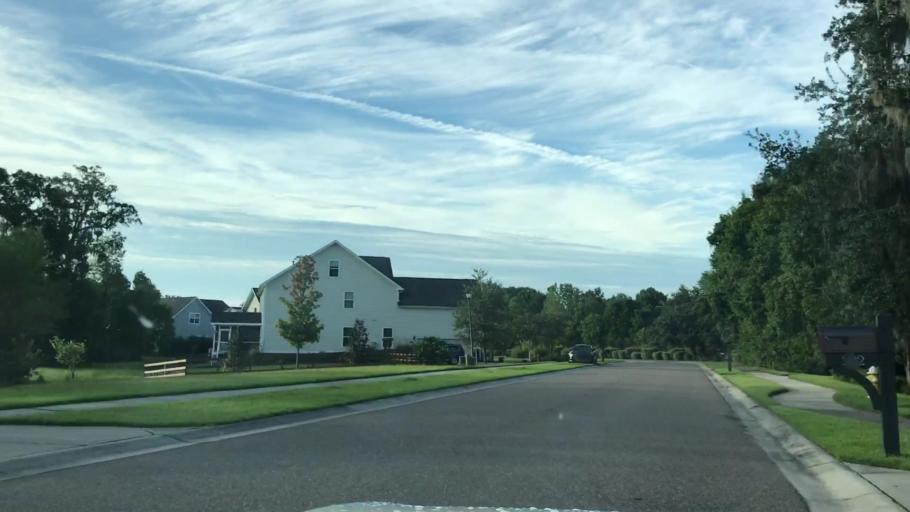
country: US
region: South Carolina
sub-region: Charleston County
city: Shell Point
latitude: 32.8400
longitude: -80.0809
